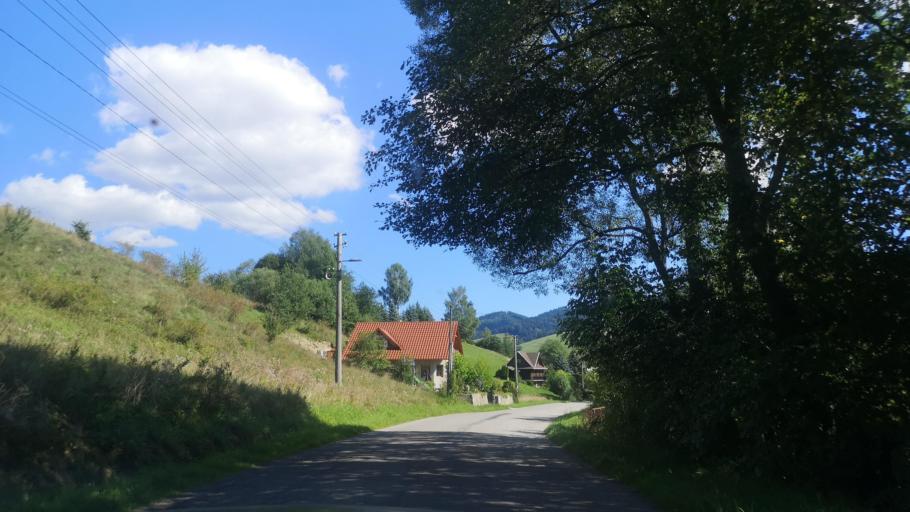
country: SK
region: Zilinsky
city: Oravska Lesna
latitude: 49.2741
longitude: 19.1397
